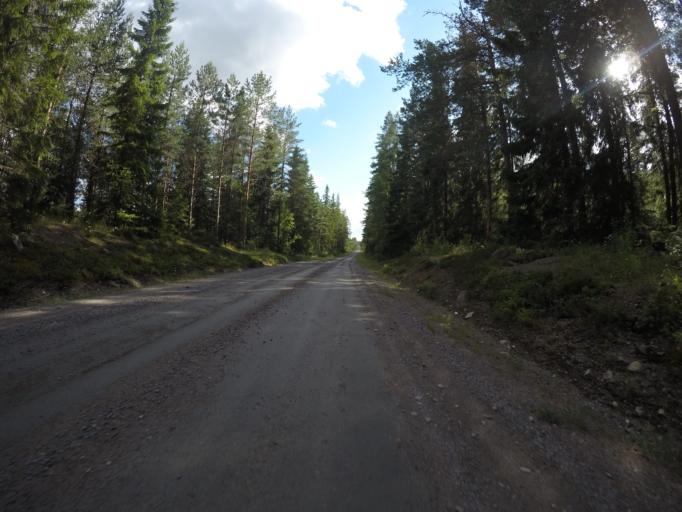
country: SE
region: OErebro
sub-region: Hallefors Kommun
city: Haellefors
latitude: 59.9235
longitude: 14.6028
